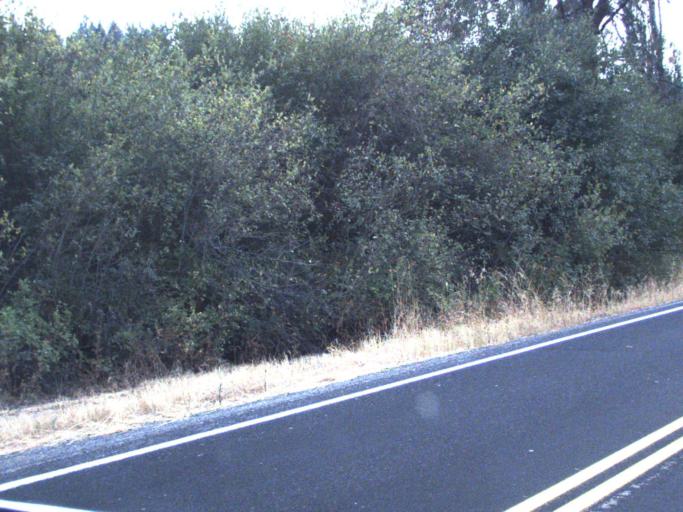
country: US
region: Washington
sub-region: Spokane County
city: Trentwood
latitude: 47.8025
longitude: -117.2172
